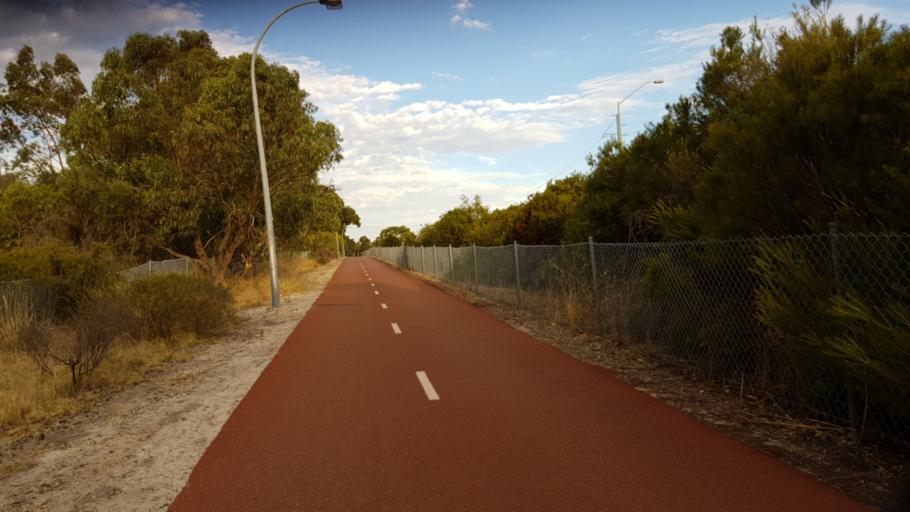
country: AU
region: Western Australia
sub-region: Canning
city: Canning Vale
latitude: -32.0542
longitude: 115.9127
